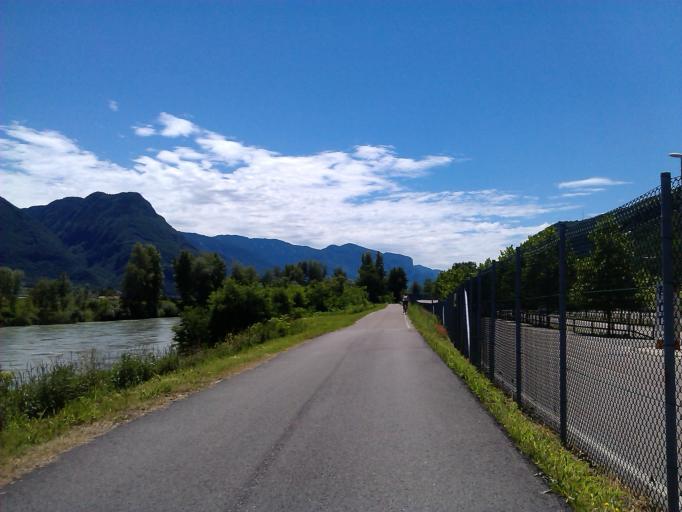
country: IT
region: Trentino-Alto Adige
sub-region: Bolzano
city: Laives
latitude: 46.4362
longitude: 11.3155
